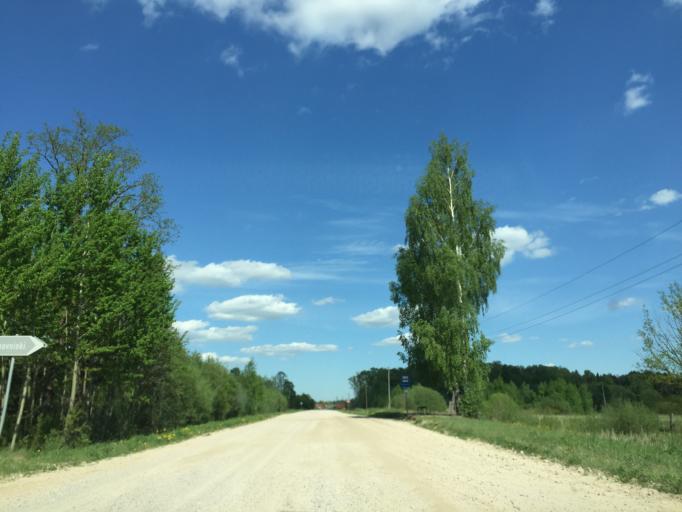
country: LV
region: Bauskas Rajons
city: Bauska
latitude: 56.3916
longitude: 24.1001
